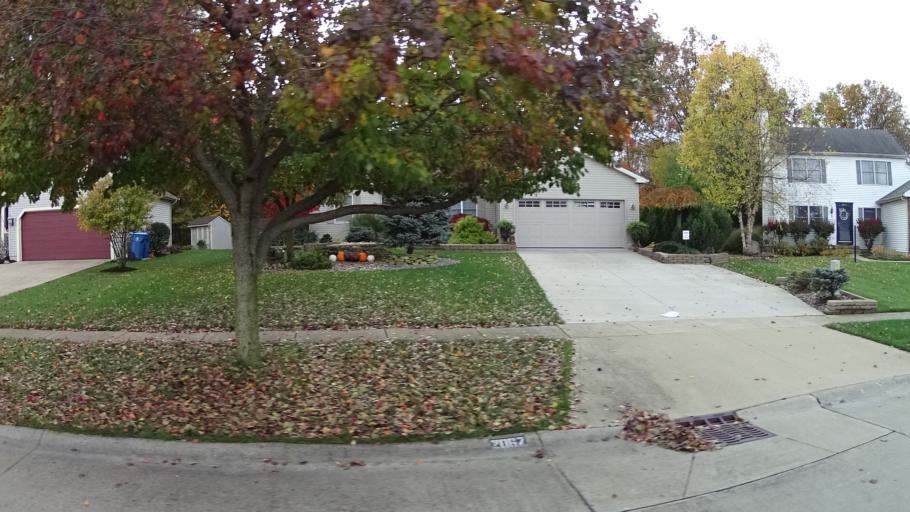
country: US
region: Ohio
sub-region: Lorain County
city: Amherst
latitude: 41.4228
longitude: -82.2060
